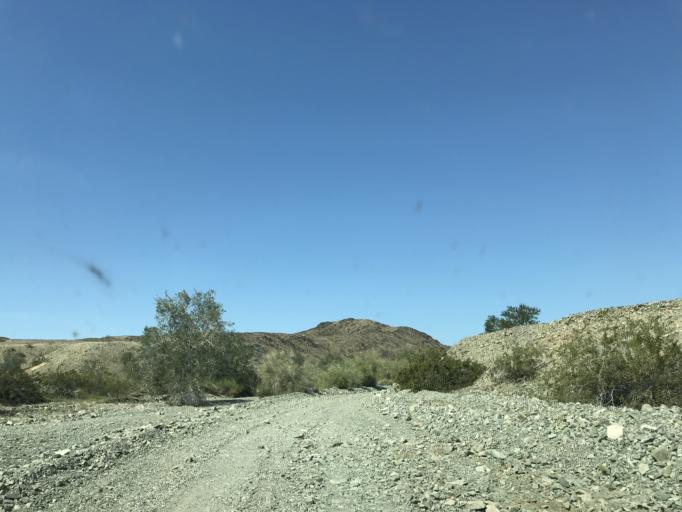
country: US
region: California
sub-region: Riverside County
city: Mesa Verde
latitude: 33.4948
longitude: -114.8322
